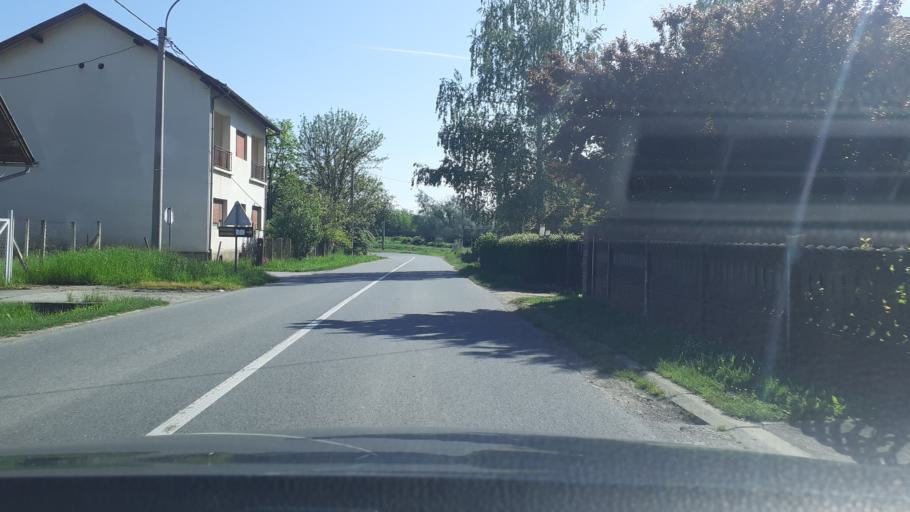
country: HR
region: Pozesko-Slavonska
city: Jaksic
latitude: 45.3280
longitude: 17.7554
